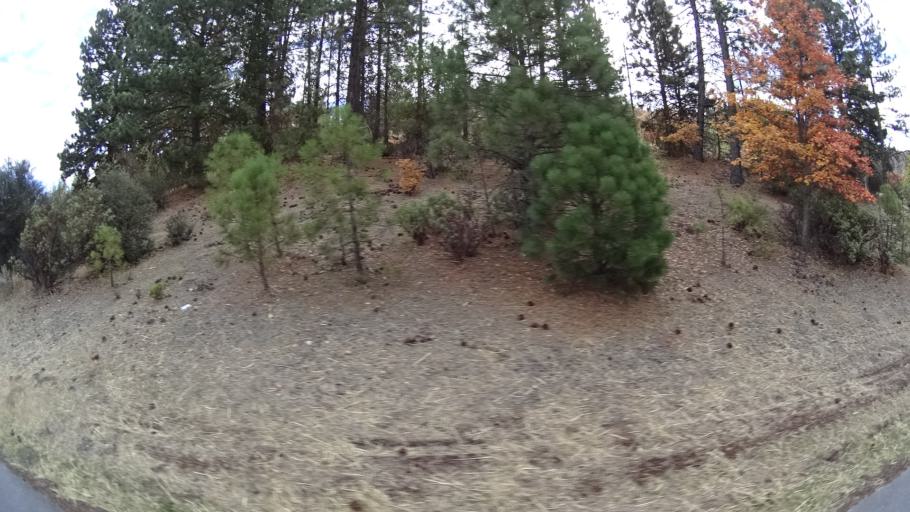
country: US
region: California
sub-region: Siskiyou County
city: Yreka
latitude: 41.6247
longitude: -122.8266
